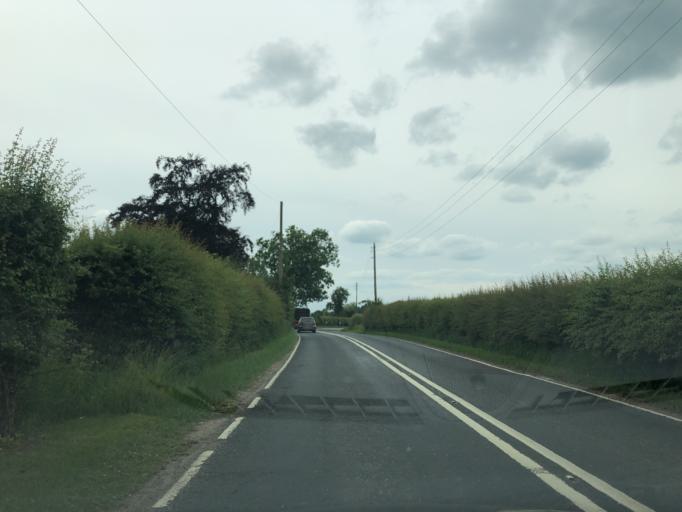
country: GB
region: England
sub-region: North Yorkshire
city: Angram Grange
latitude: 54.2346
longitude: -1.2499
